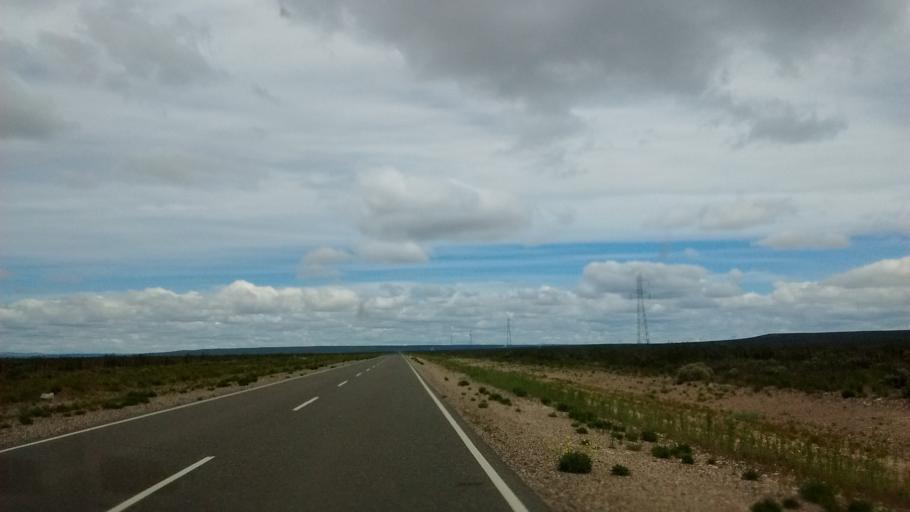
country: AR
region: Neuquen
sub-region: Departamento de Picun Leufu
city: Picun Leufu
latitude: -39.6742
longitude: -69.4494
